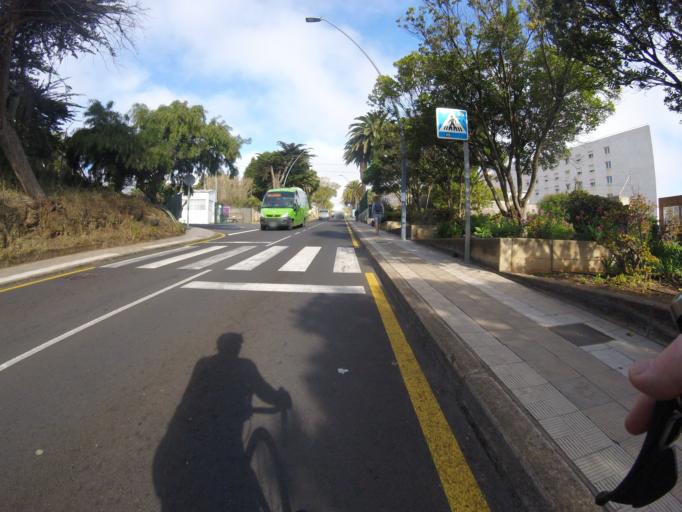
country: ES
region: Canary Islands
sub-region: Provincia de Santa Cruz de Tenerife
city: La Laguna
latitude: 28.4811
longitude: -16.3201
